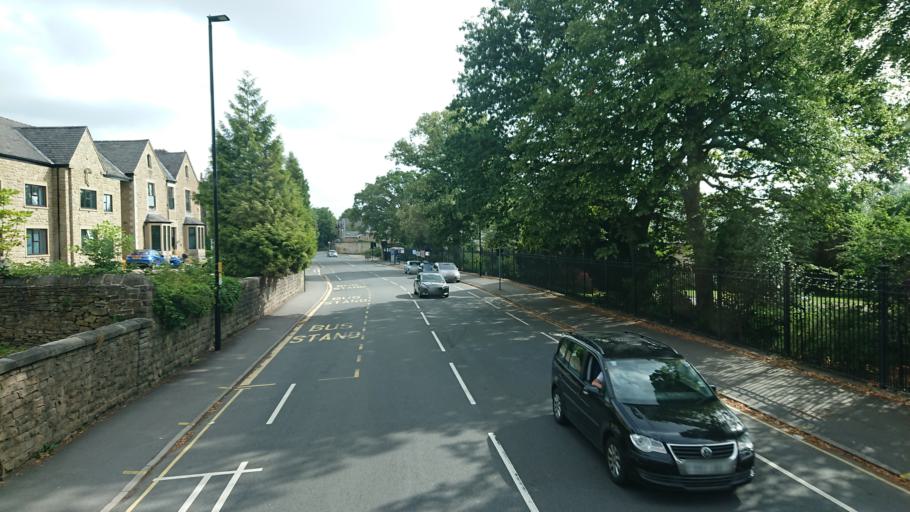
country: GB
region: England
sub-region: Sheffield
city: Sheffield
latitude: 53.3727
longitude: -1.4999
